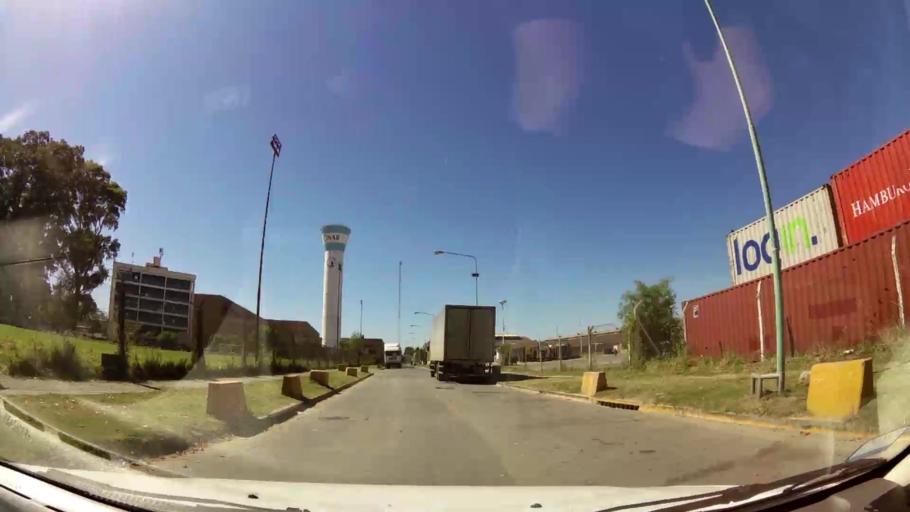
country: AR
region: Buenos Aires F.D.
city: Buenos Aires
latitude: -34.6245
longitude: -58.3536
